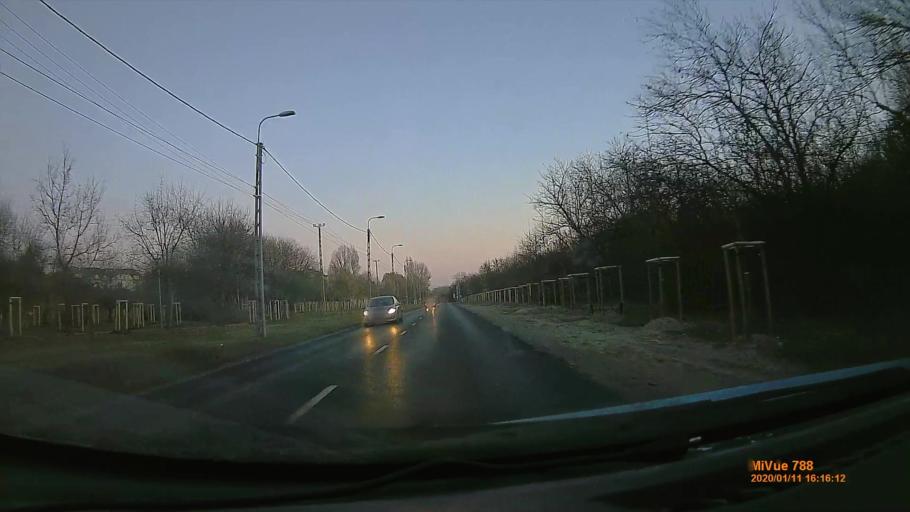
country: HU
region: Budapest
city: Budapest XVI. keruelet
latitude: 47.5276
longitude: 19.1984
